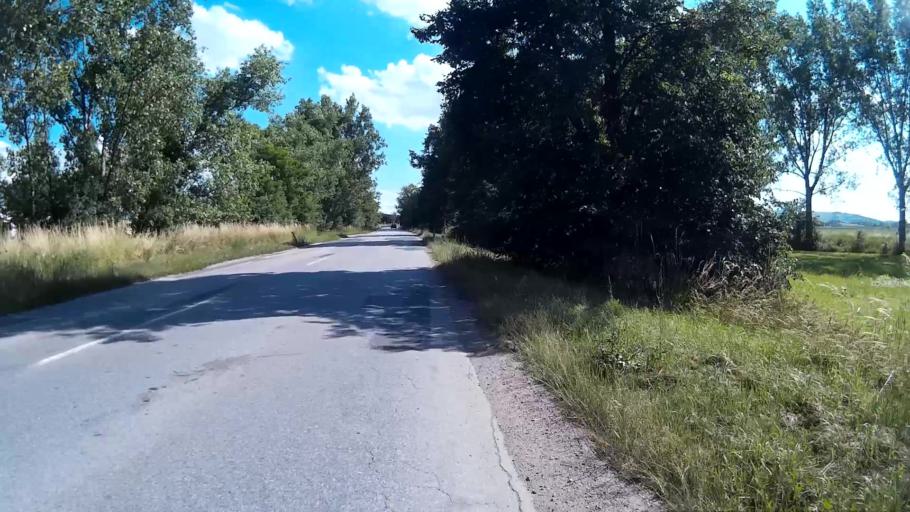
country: CZ
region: South Moravian
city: Menin
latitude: 49.0740
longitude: 16.6931
